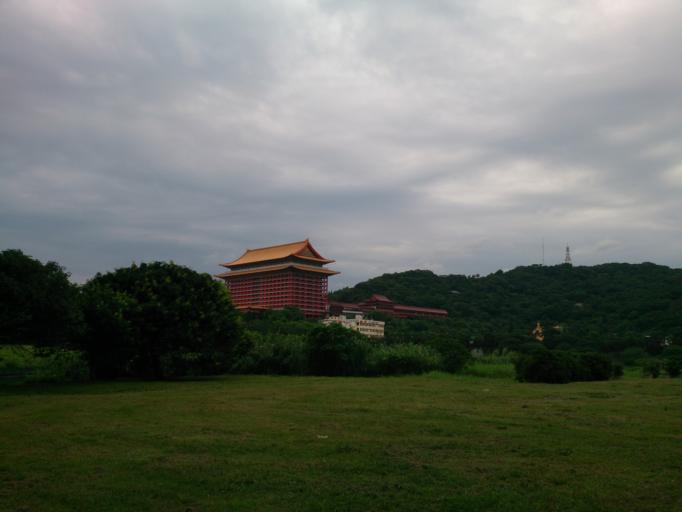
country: TW
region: Taipei
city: Taipei
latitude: 25.0742
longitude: 121.5289
